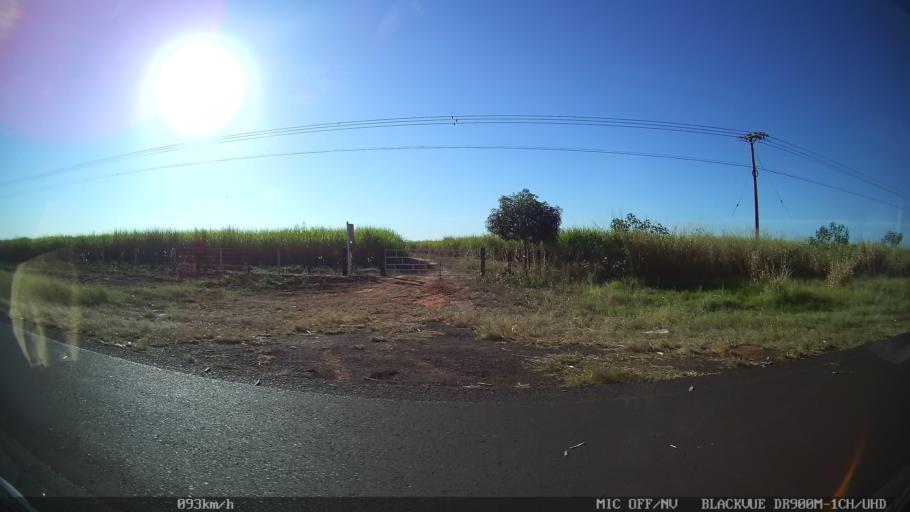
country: BR
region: Sao Paulo
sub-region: Olimpia
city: Olimpia
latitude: -20.7186
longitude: -49.0079
